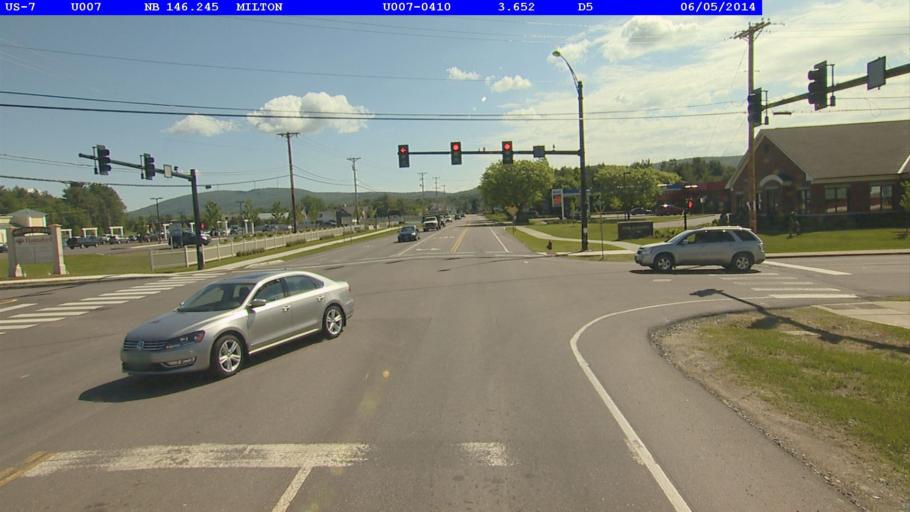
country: US
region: Vermont
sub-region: Chittenden County
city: Milton
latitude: 44.6222
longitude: -73.1228
